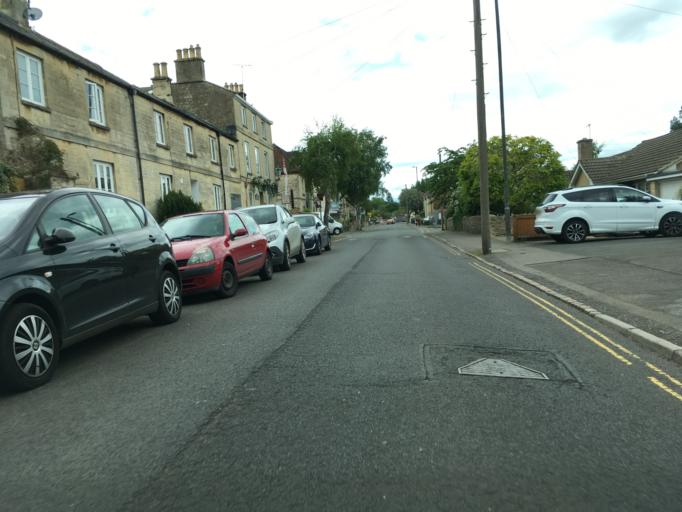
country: GB
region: England
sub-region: Gloucestershire
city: Cirencester
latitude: 51.7143
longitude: -1.9615
